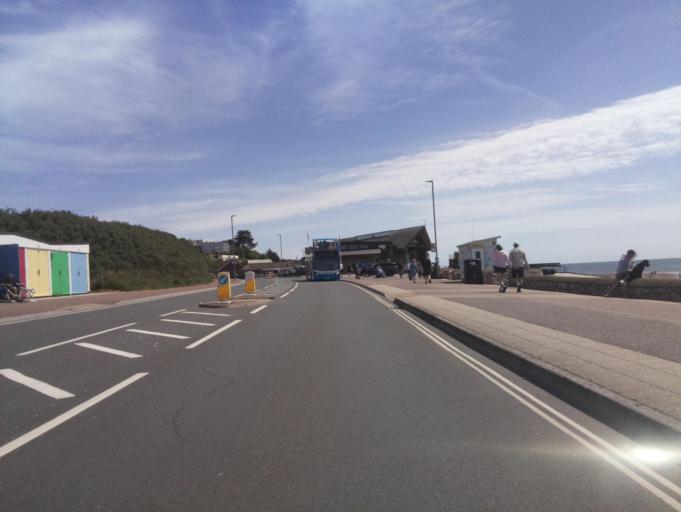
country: GB
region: England
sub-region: Devon
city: Exmouth
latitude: 50.6118
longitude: -3.4003
